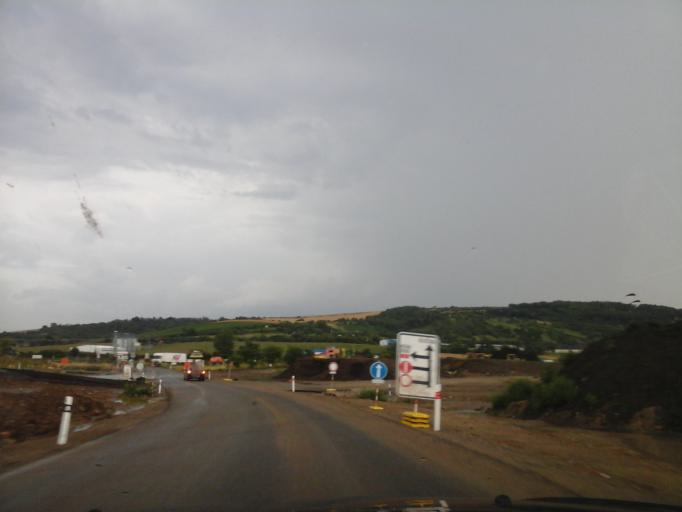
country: CZ
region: South Moravian
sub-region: Okres Brno-Venkov
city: Blucina
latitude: 49.0585
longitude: 16.6658
